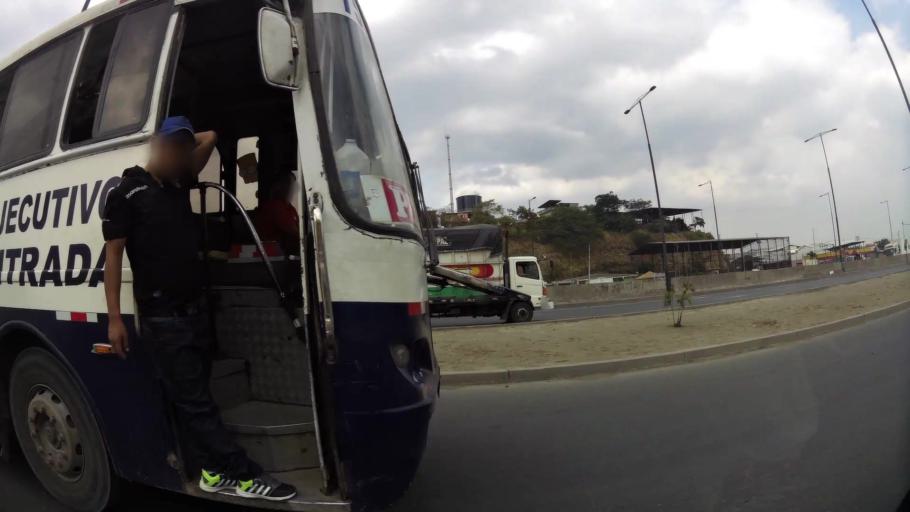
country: EC
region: Guayas
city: Santa Lucia
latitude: -2.1167
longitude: -79.9486
